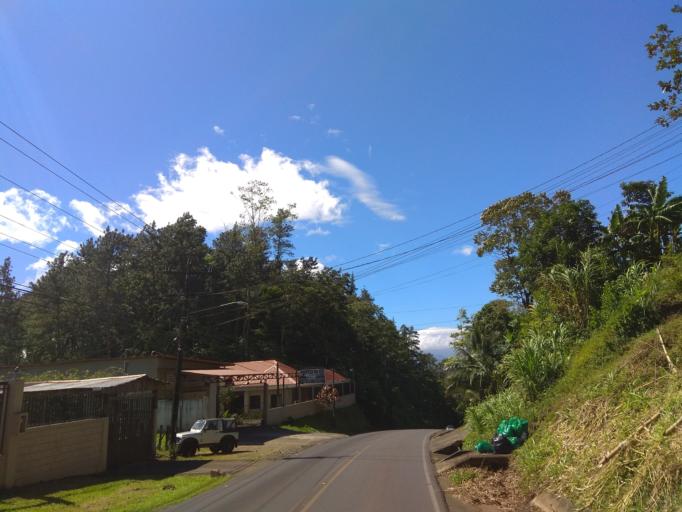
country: CR
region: Alajuela
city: Quesada
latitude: 10.3574
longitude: -84.4558
